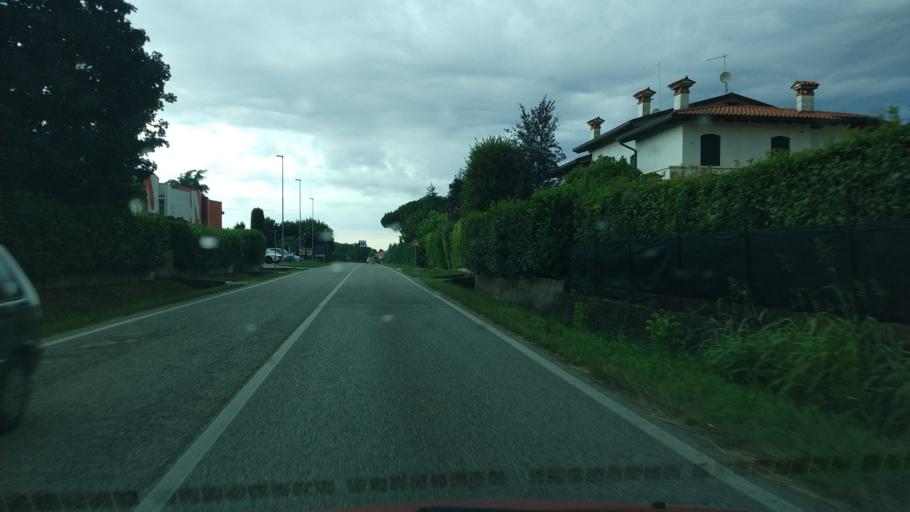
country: IT
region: Veneto
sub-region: Provincia di Vicenza
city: Zugliano
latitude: 45.7334
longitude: 11.5246
